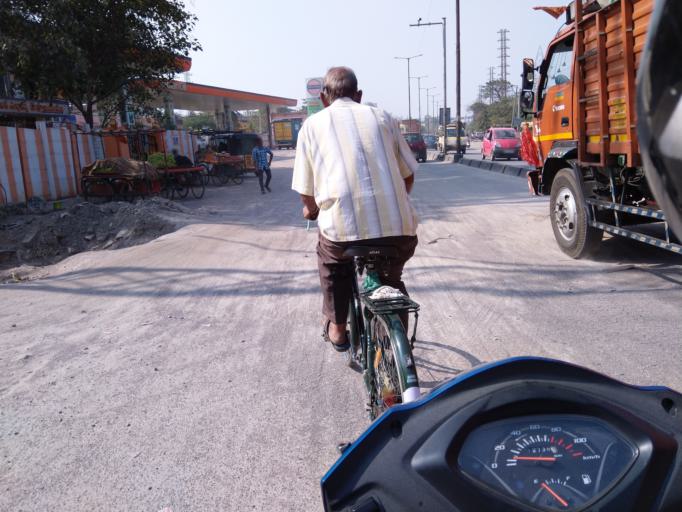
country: IN
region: Telangana
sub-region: Rangareddi
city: Quthbullapur
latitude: 17.5268
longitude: 78.4398
